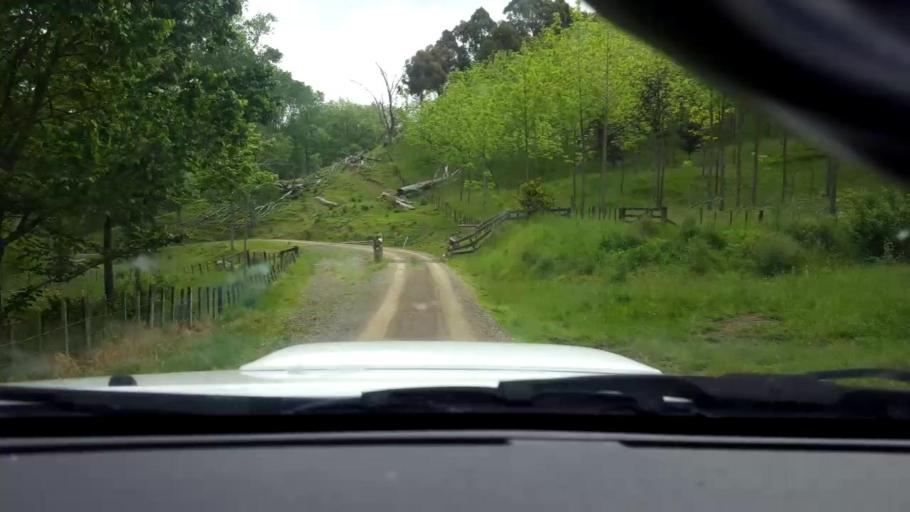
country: NZ
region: Gisborne
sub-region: Gisborne District
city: Gisborne
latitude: -38.4885
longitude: 177.6863
